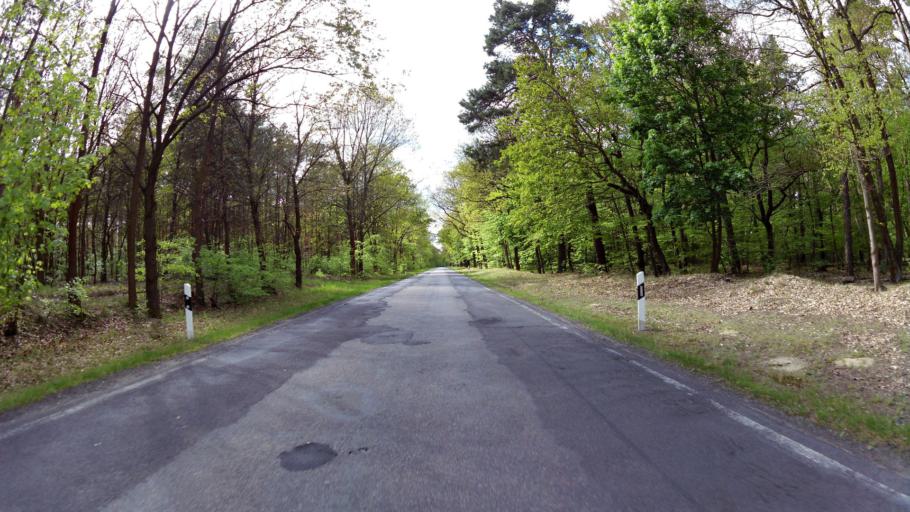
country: DE
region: Brandenburg
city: Furstenwalde
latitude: 52.3591
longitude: 14.0372
